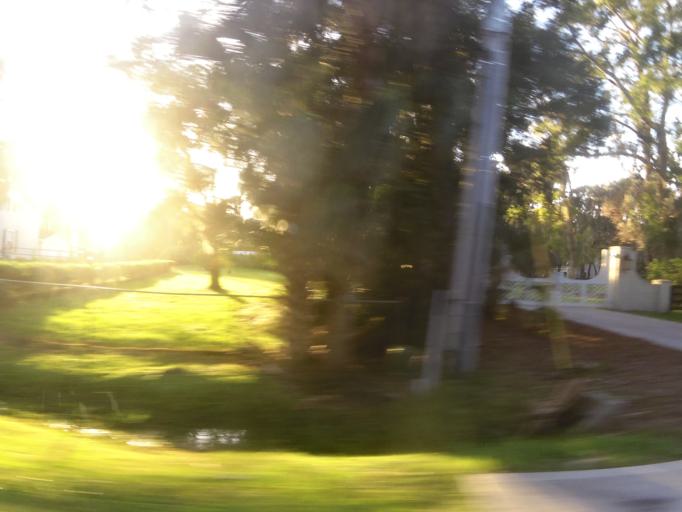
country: US
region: Florida
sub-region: Saint Johns County
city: Palm Valley
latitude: 30.1701
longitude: -81.3862
